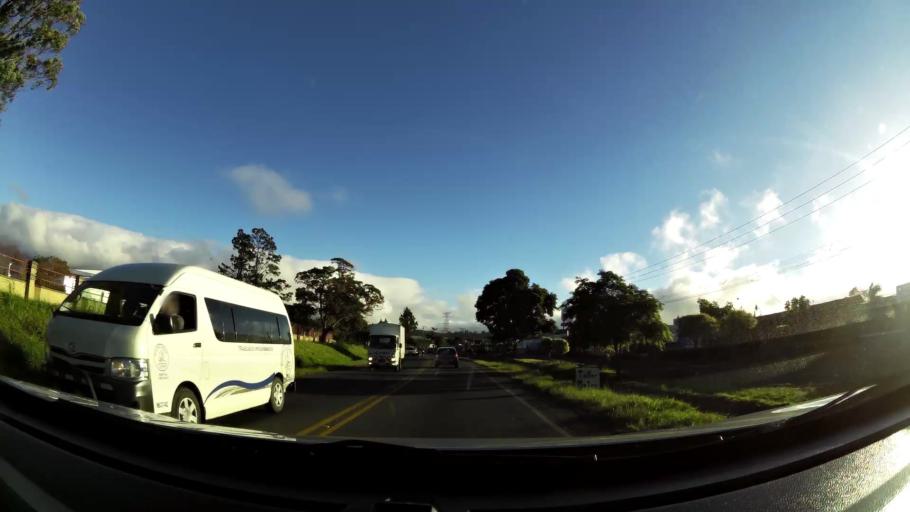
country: CR
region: Heredia
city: Angeles
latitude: 9.9927
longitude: -84.0382
